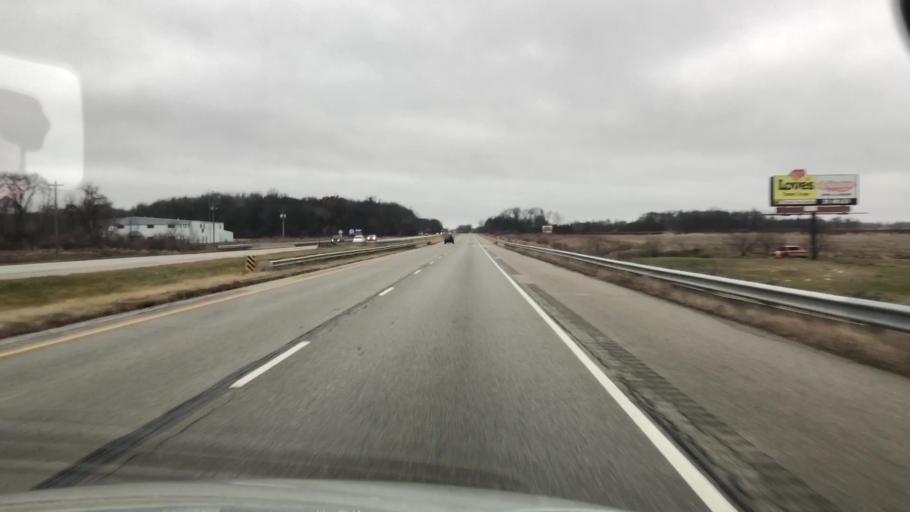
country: US
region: Indiana
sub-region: Kosciusko County
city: Mentone
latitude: 41.2676
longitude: -85.9995
